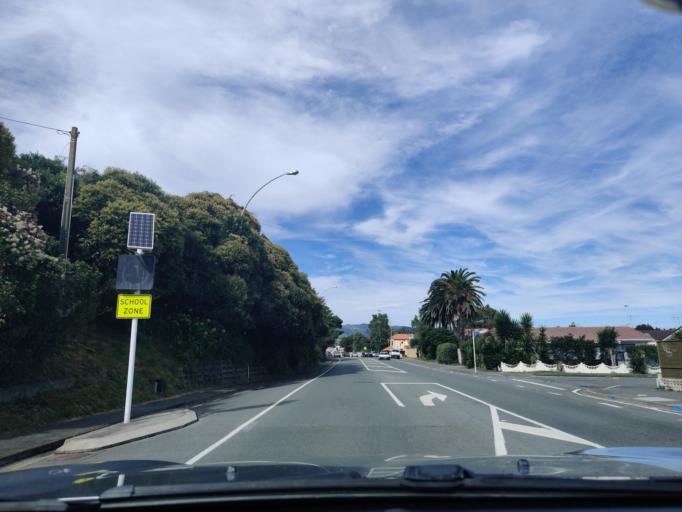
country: NZ
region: Nelson
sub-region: Nelson City
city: Nelson
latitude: -41.2846
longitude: 173.2481
